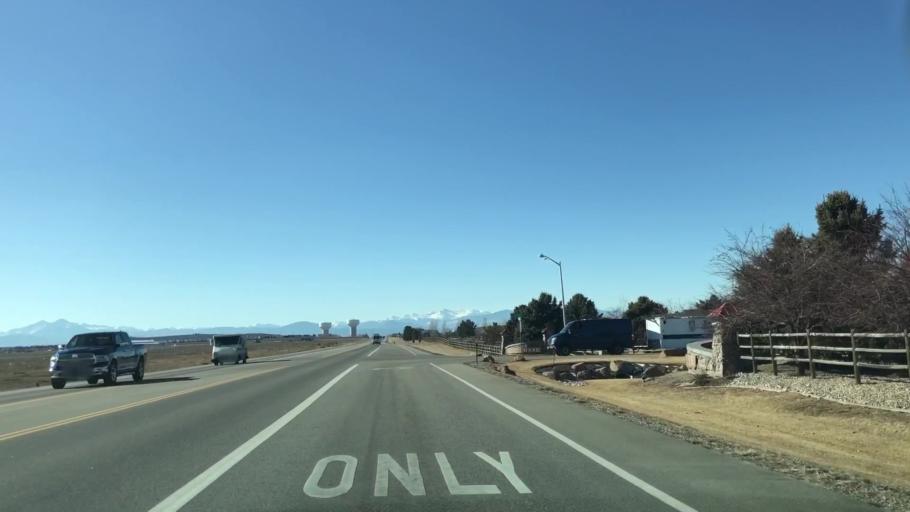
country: US
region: Colorado
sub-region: Weld County
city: Windsor
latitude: 40.4360
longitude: -104.9508
